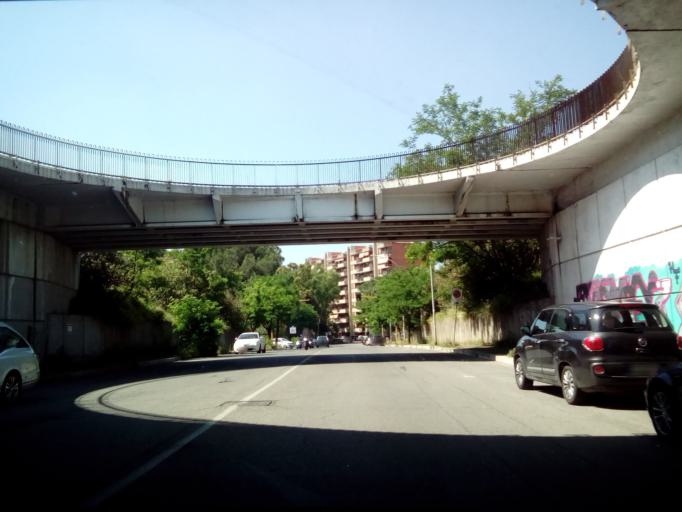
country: IT
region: Latium
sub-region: Citta metropolitana di Roma Capitale
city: Rome
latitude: 41.8887
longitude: 12.5867
